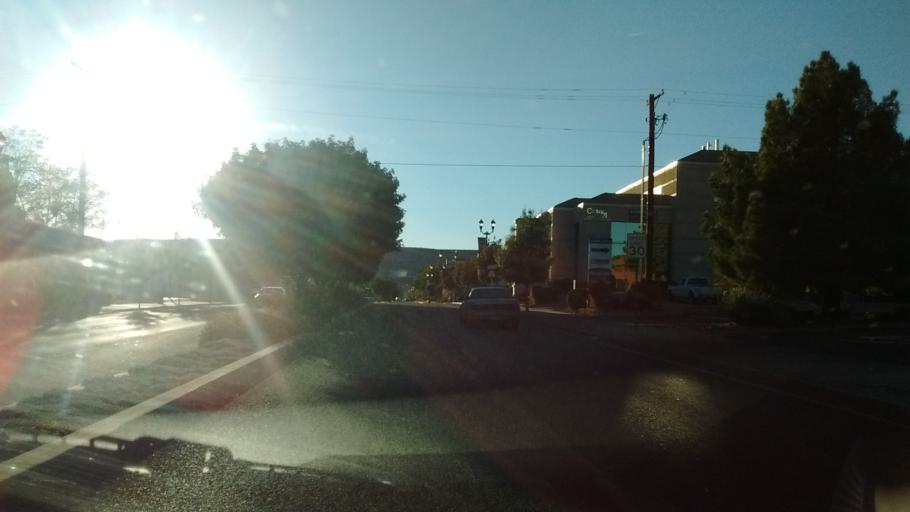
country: US
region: Utah
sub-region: Washington County
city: Saint George
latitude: 37.1100
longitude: -113.5754
